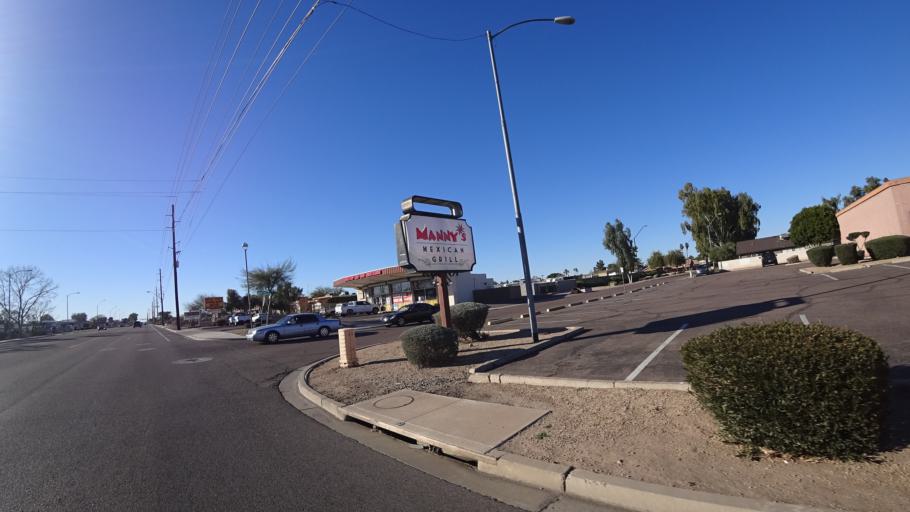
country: US
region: Arizona
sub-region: Maricopa County
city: Avondale
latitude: 33.4499
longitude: -112.3450
